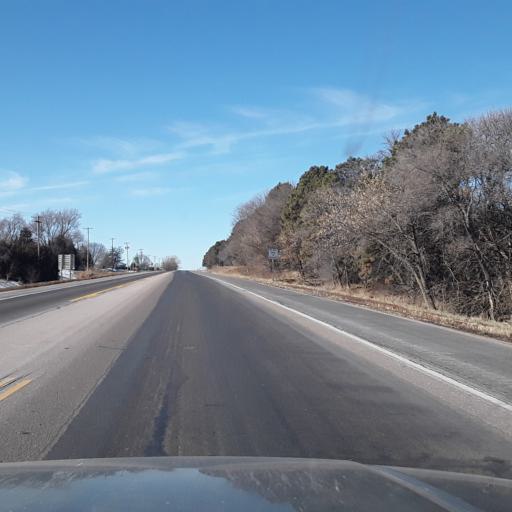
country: US
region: Nebraska
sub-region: Adams County
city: Hastings
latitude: 40.5681
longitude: -98.4421
